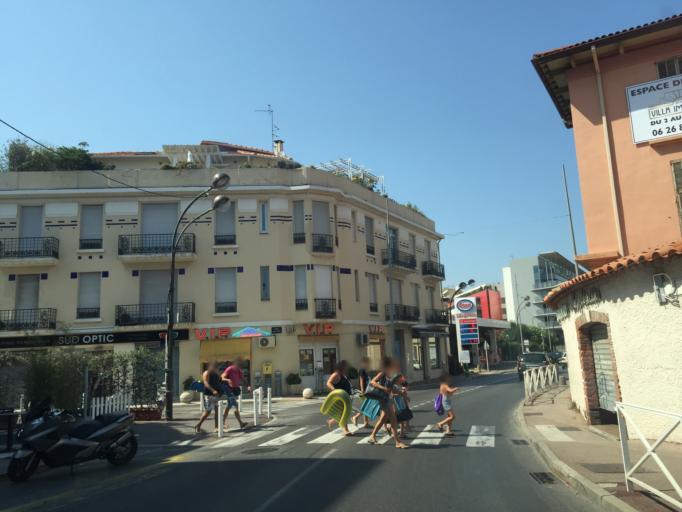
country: FR
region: Provence-Alpes-Cote d'Azur
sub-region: Departement des Alpes-Maritimes
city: Antibes
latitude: 43.5738
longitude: 7.1241
